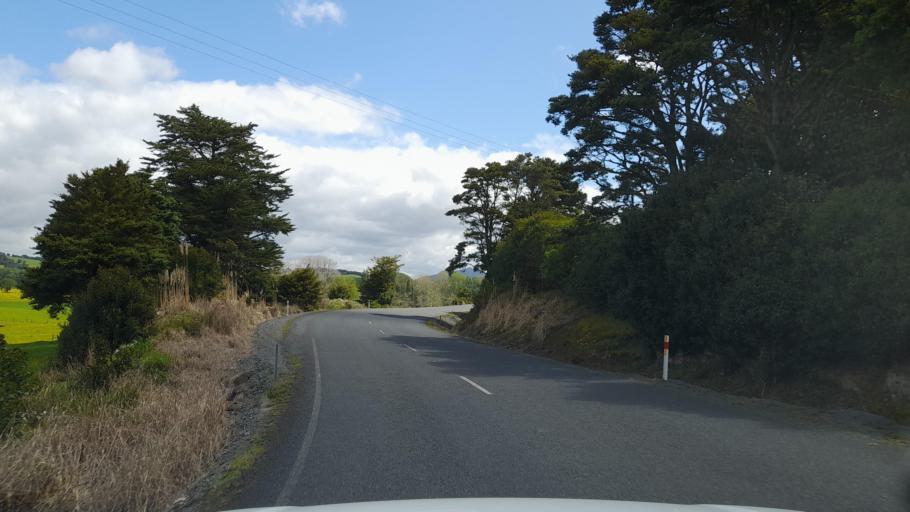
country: NZ
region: Northland
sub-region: Whangarei
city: Maungatapere
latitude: -35.7108
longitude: 174.0550
